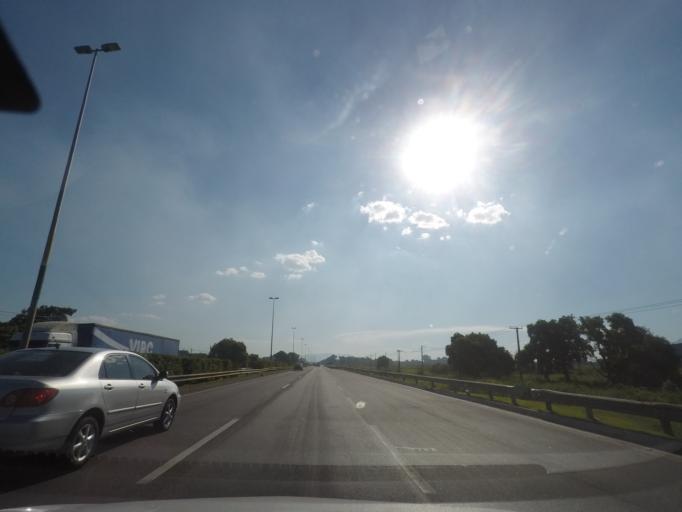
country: BR
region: Rio de Janeiro
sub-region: Duque De Caxias
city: Duque de Caxias
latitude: -22.6564
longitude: -43.2461
